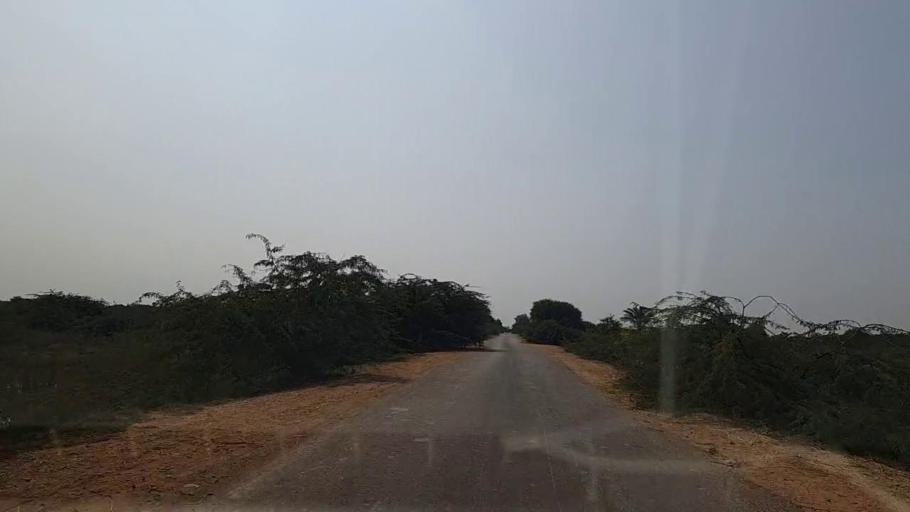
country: PK
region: Sindh
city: Chuhar Jamali
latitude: 24.2699
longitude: 67.9122
